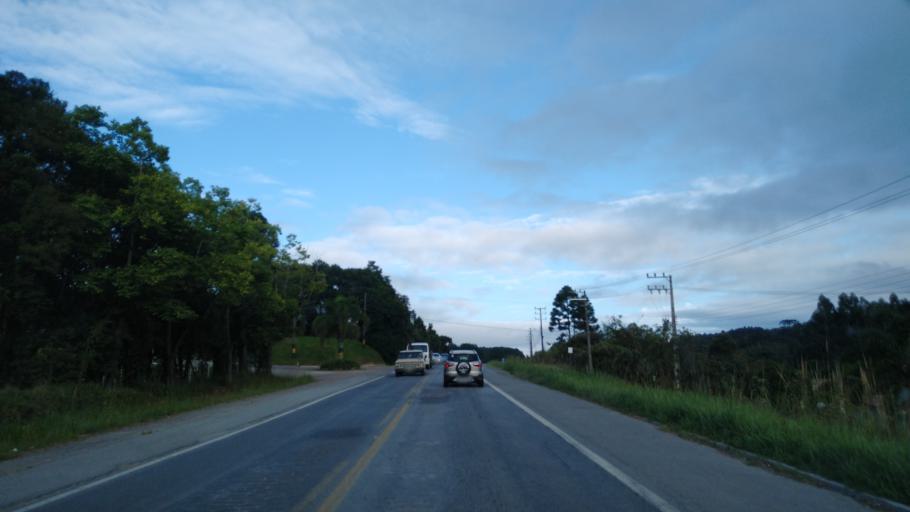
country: BR
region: Santa Catarina
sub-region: Rio Negrinho
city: Rio Negrinho
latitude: -26.2422
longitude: -49.4728
